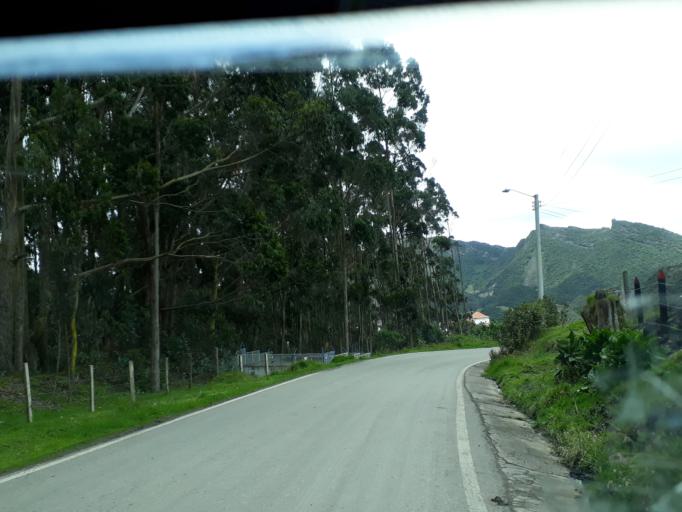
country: CO
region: Cundinamarca
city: Sutatausa
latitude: 5.1946
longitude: -73.8975
